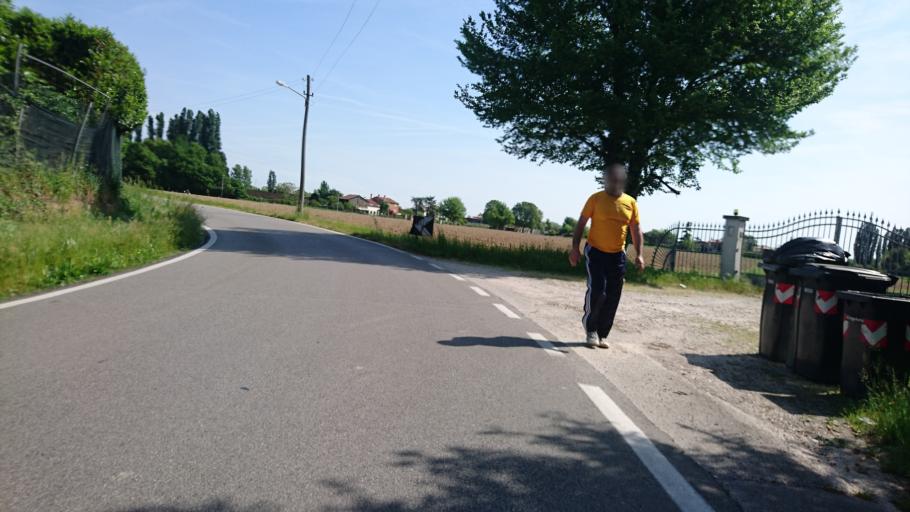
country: IT
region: Veneto
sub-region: Provincia di Padova
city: Mejaniga
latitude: 45.4331
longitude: 11.9019
